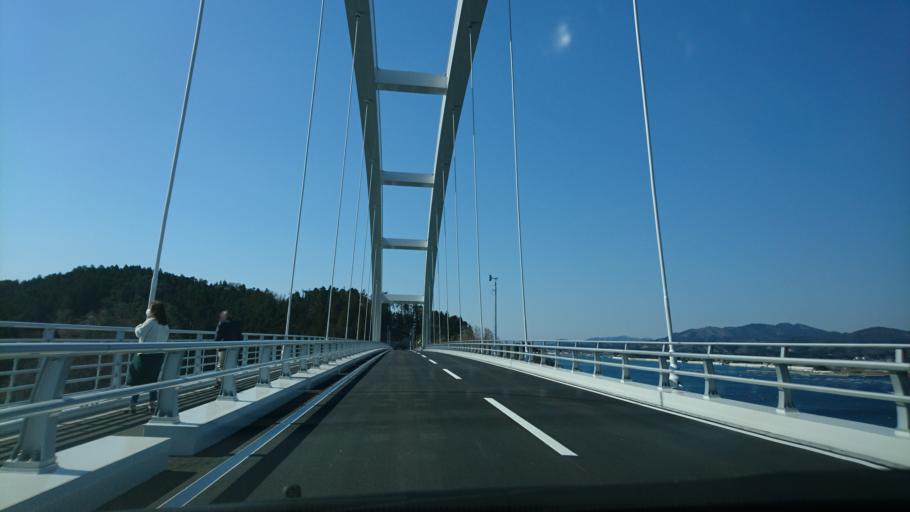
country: JP
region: Iwate
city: Ofunato
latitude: 38.8793
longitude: 141.6064
